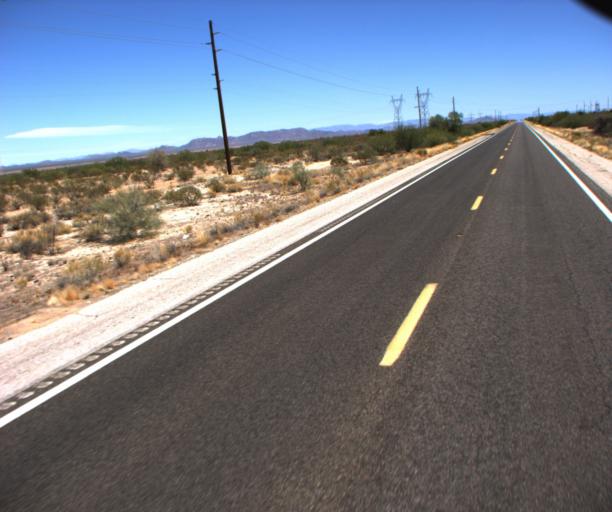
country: US
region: Arizona
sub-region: La Paz County
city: Salome
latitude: 33.9038
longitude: -113.2961
